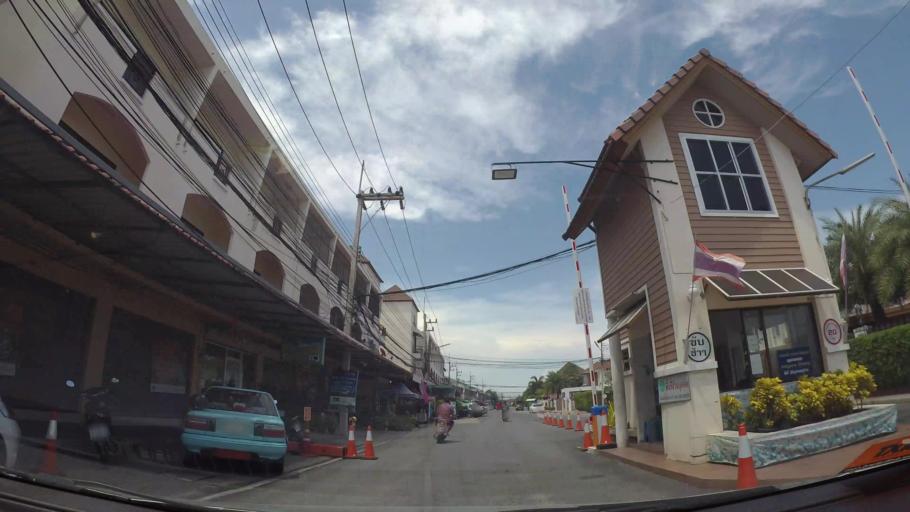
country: TH
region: Chon Buri
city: Chon Buri
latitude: 13.3299
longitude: 100.9457
